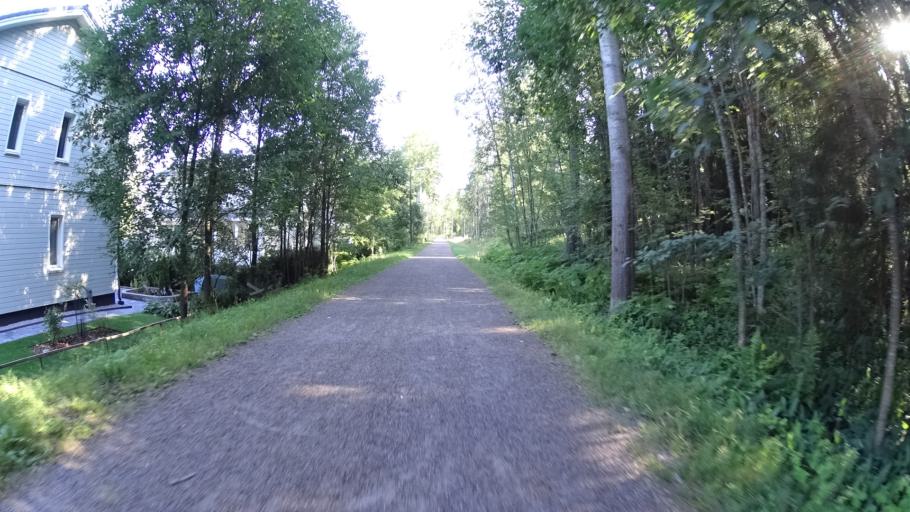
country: FI
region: Uusimaa
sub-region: Helsinki
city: Kilo
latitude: 60.2372
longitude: 24.8246
